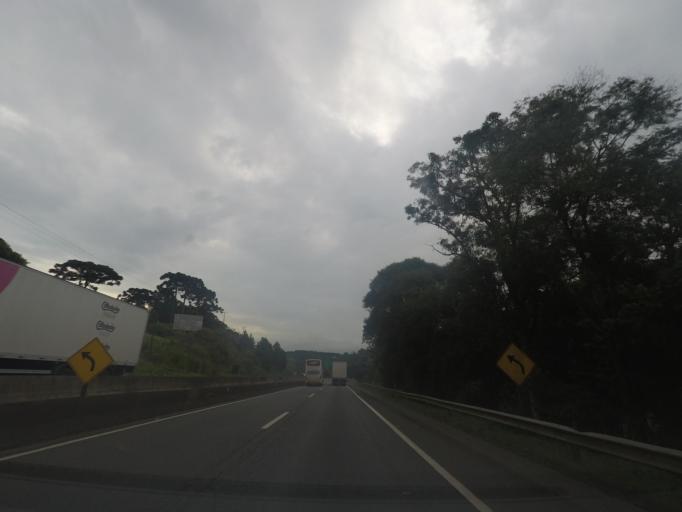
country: BR
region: Parana
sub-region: Campina Grande Do Sul
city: Campina Grande do Sul
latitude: -25.3107
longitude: -49.0064
